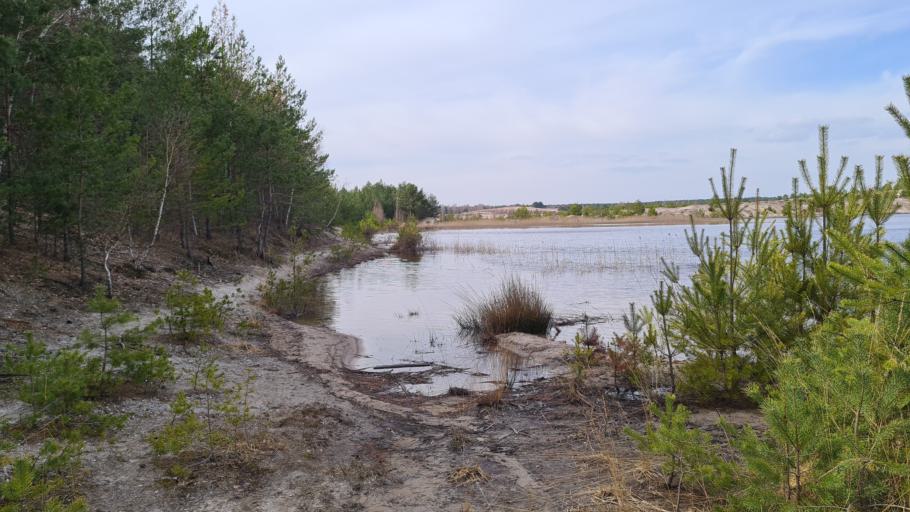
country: DE
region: Brandenburg
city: Lauchhammer
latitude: 51.5413
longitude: 13.7158
